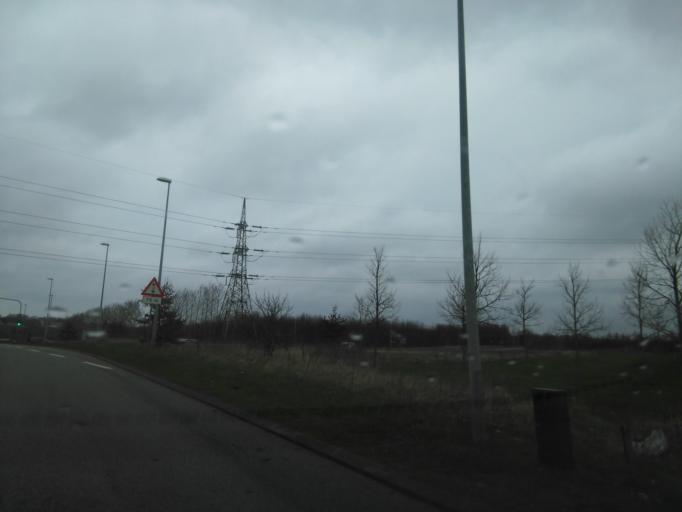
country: DK
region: Central Jutland
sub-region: Arhus Kommune
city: Stavtrup
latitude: 56.1652
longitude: 10.0949
